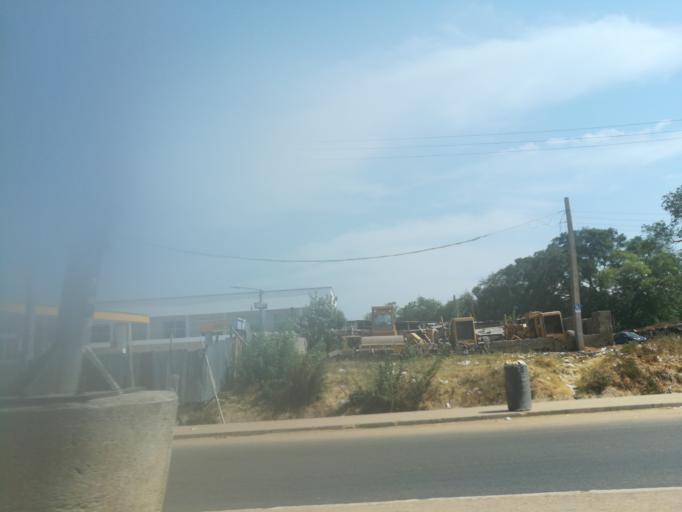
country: NG
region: Kano
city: Kano
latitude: 12.0233
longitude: 8.5159
